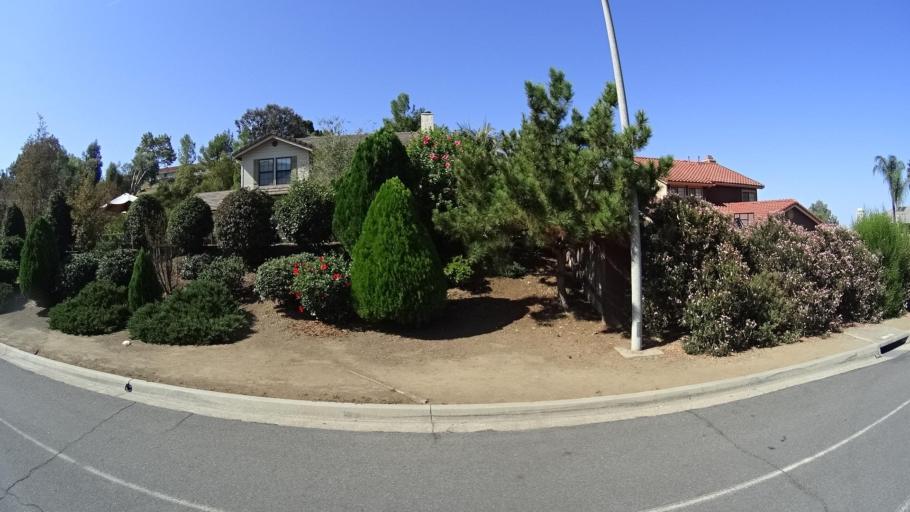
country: US
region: California
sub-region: San Diego County
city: Granite Hills
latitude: 32.7957
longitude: -116.9020
